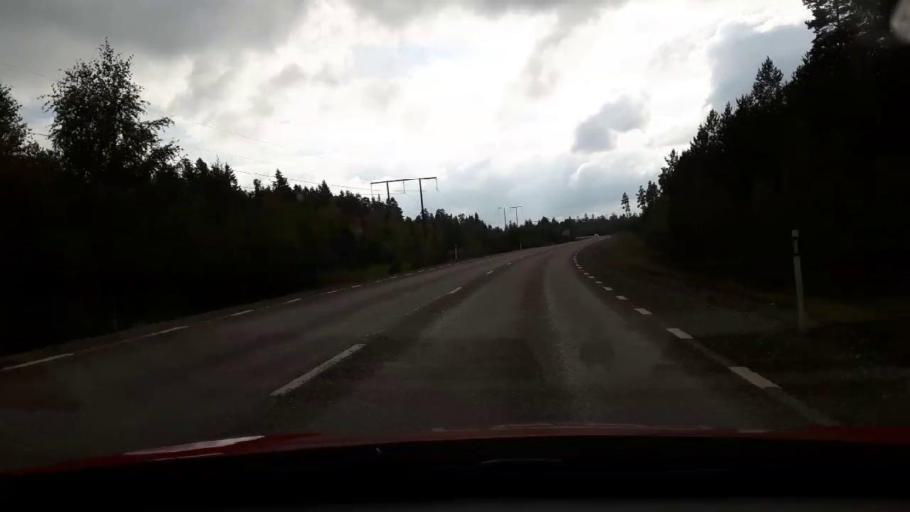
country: SE
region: Gaevleborg
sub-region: Soderhamns Kommun
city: Ljusne
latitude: 61.0947
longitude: 16.9546
